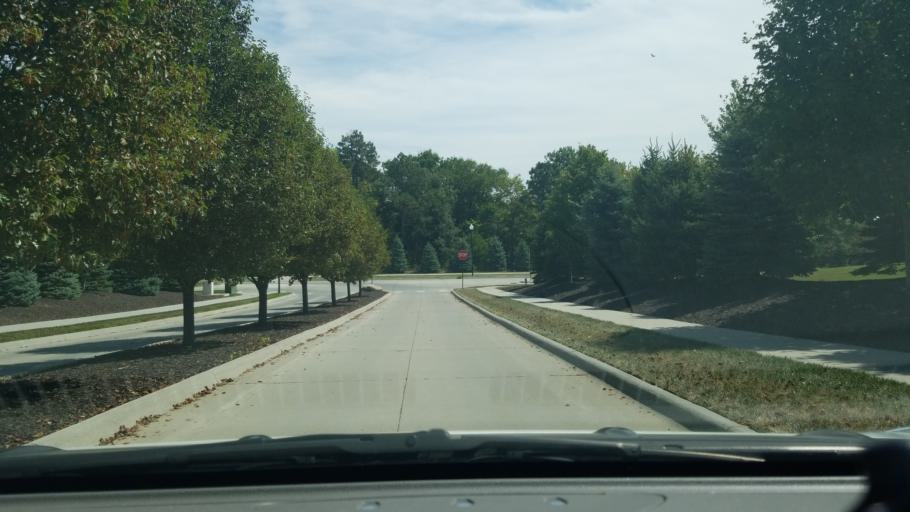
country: US
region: Nebraska
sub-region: Sarpy County
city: Papillion
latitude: 41.1438
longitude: -96.1017
